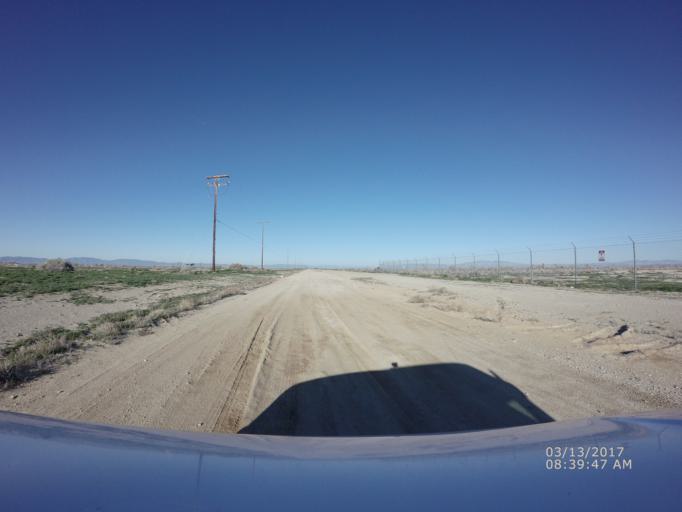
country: US
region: California
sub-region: Los Angeles County
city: Lake Los Angeles
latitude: 34.7341
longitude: -117.9603
